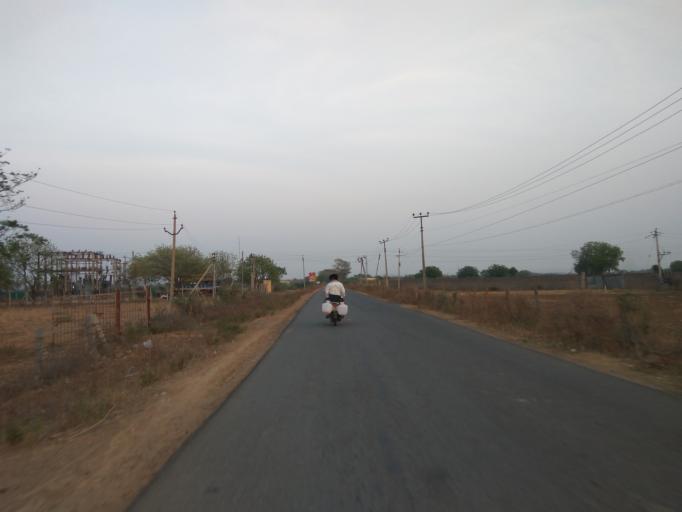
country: IN
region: Andhra Pradesh
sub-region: Prakasam
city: Markapur
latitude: 15.7524
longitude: 79.2274
